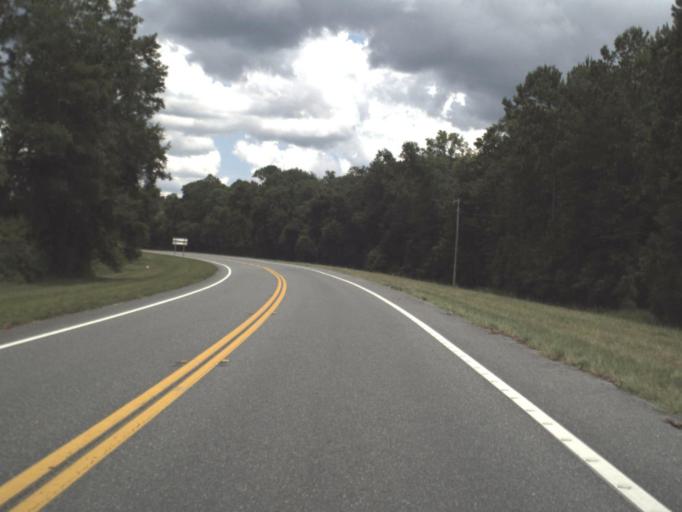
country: US
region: Florida
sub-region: Taylor County
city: Perry
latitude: 30.0820
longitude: -83.5022
